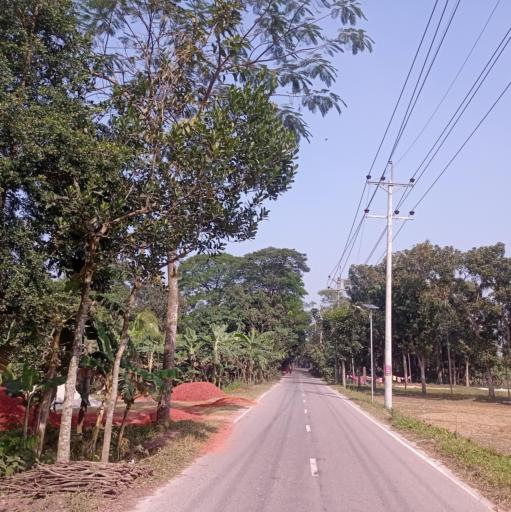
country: BD
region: Dhaka
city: Narsingdi
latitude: 24.0412
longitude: 90.6782
